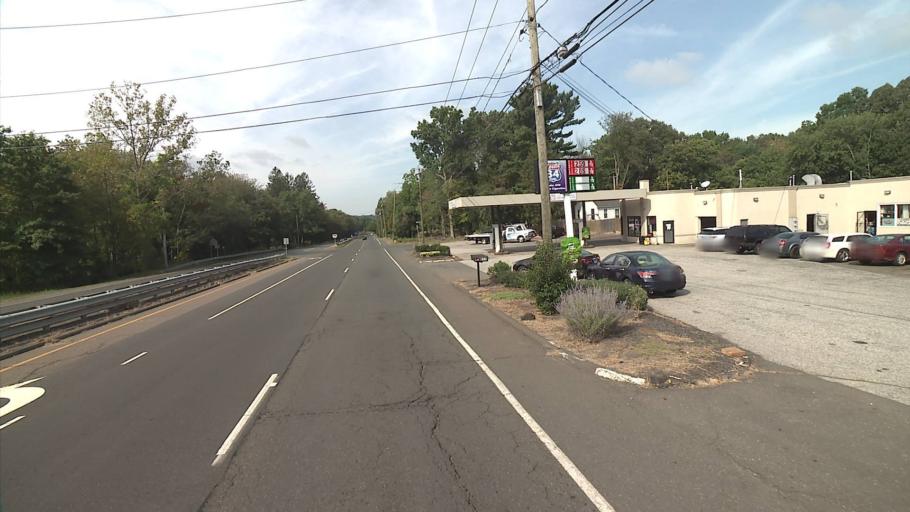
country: US
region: Connecticut
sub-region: New Haven County
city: Orange
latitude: 41.2987
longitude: -73.0038
